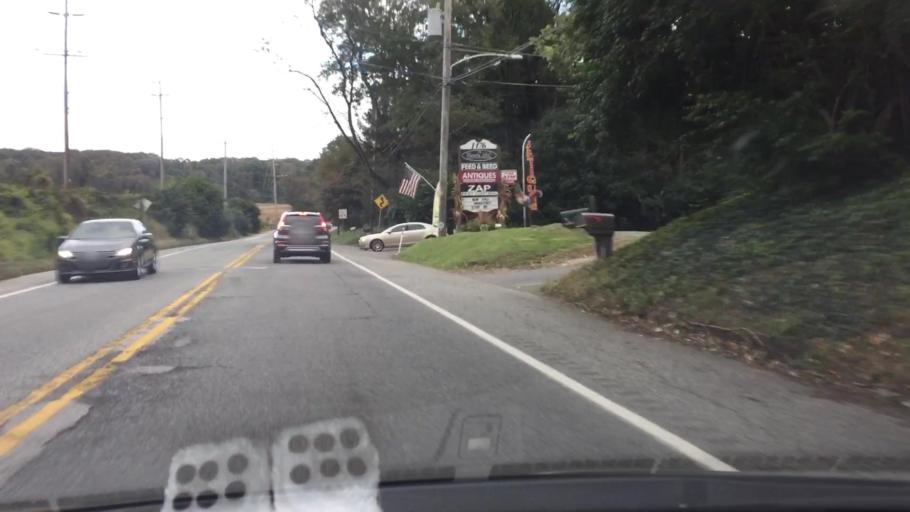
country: US
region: Pennsylvania
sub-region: Delaware County
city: Lima
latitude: 39.9388
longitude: -75.4591
